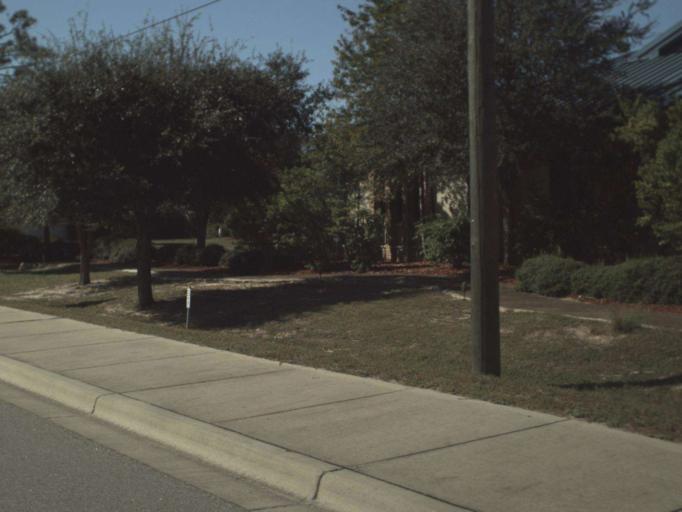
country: US
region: Florida
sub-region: Walton County
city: Seaside
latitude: 30.3745
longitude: -86.1800
